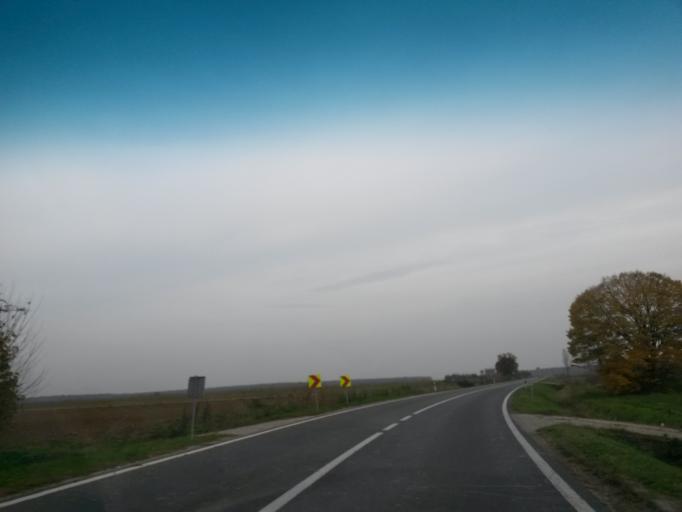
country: HR
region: Vukovarsko-Srijemska
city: Slakovci
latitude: 45.2105
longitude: 18.9968
